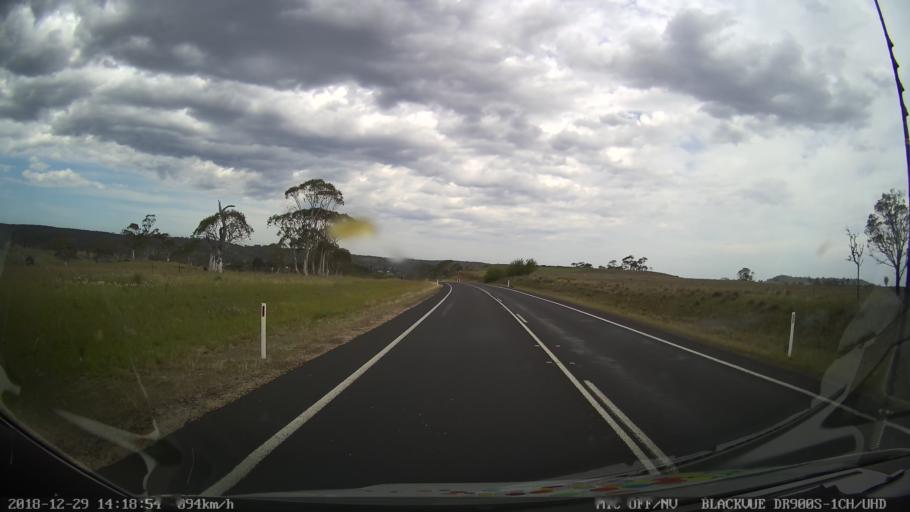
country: AU
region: New South Wales
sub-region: Cooma-Monaro
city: Cooma
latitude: -36.4933
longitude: 149.2740
